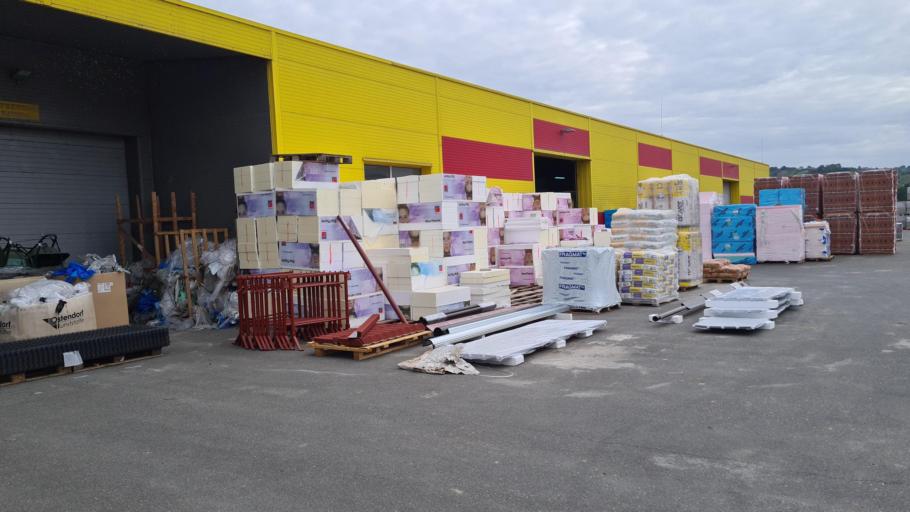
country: SI
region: Lendava-Lendva
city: Lendava
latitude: 46.5501
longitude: 16.4502
